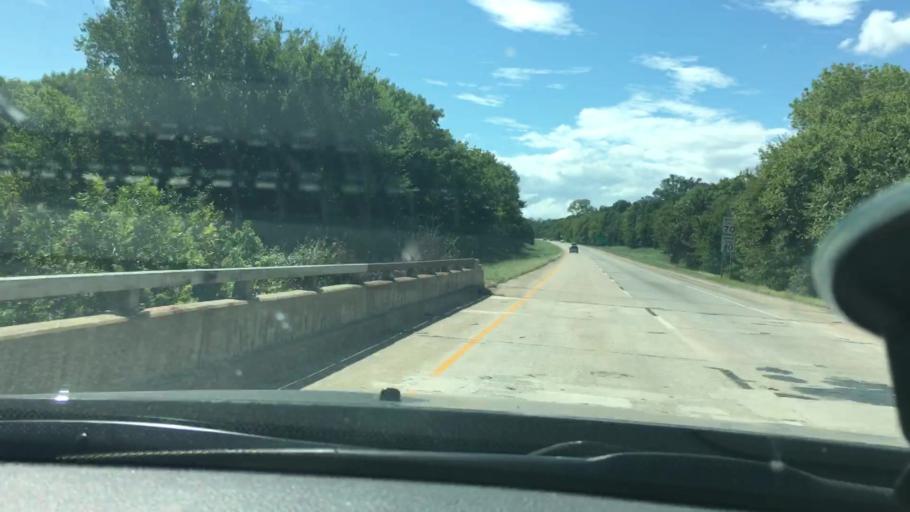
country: US
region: Oklahoma
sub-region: Sequoyah County
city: Vian
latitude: 35.4899
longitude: -94.9839
